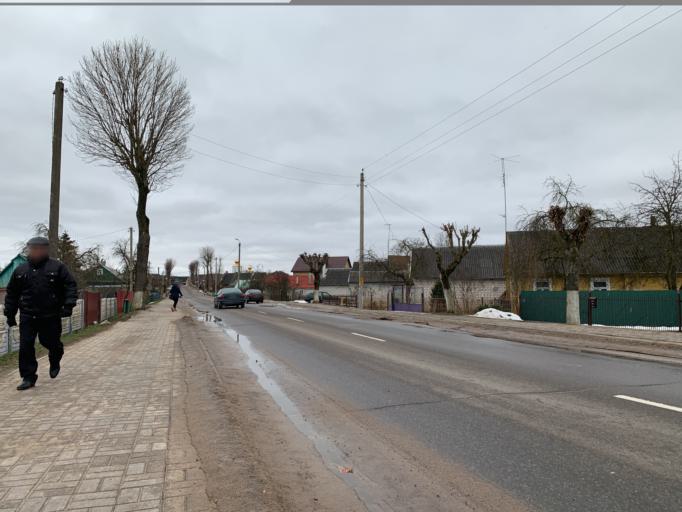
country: BY
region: Minsk
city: Nyasvizh
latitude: 53.2275
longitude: 26.6779
